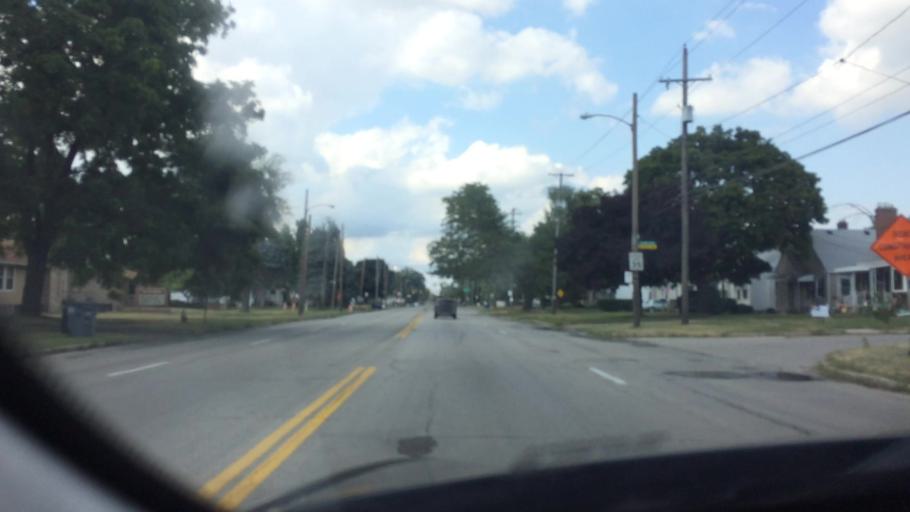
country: US
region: Ohio
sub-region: Wood County
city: Perrysburg
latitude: 41.5865
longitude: -83.6169
